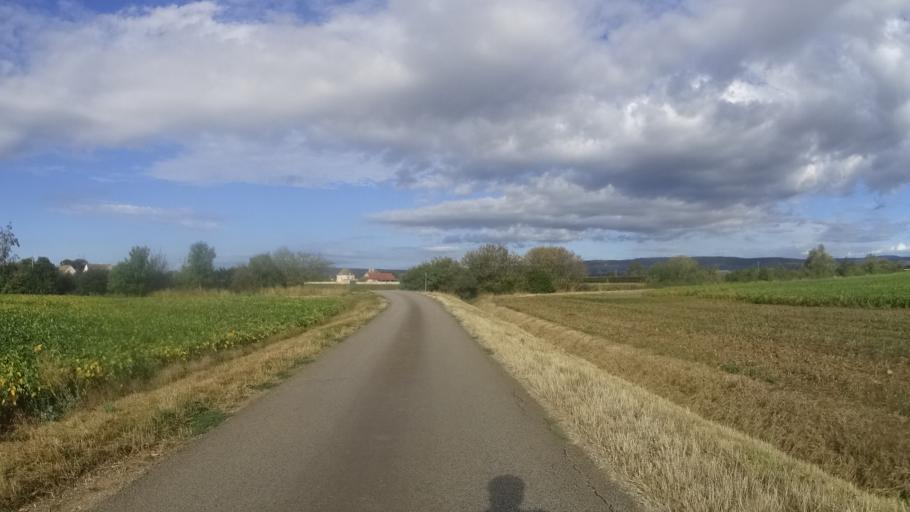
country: FR
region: Bourgogne
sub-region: Departement de Saone-et-Loire
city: Demigny
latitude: 46.9392
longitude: 4.8079
